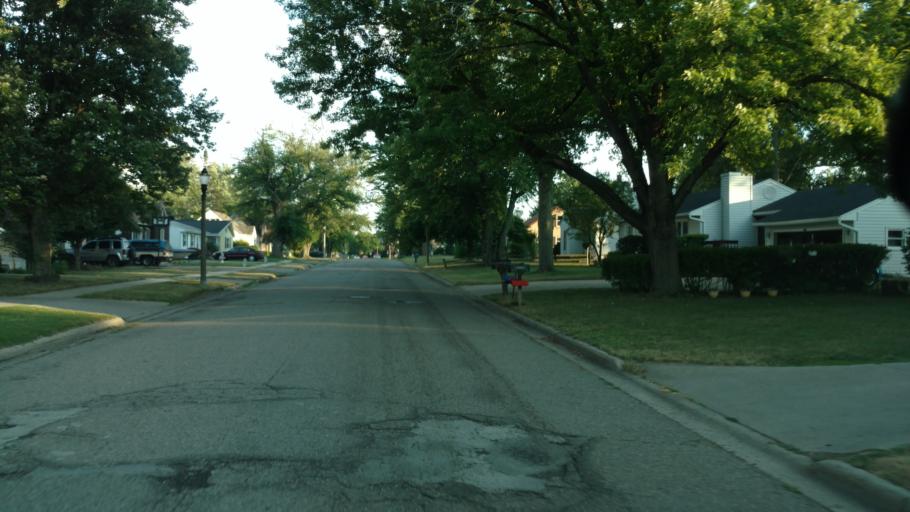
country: US
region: Michigan
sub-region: Eaton County
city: Waverly
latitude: 42.7356
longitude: -84.6133
